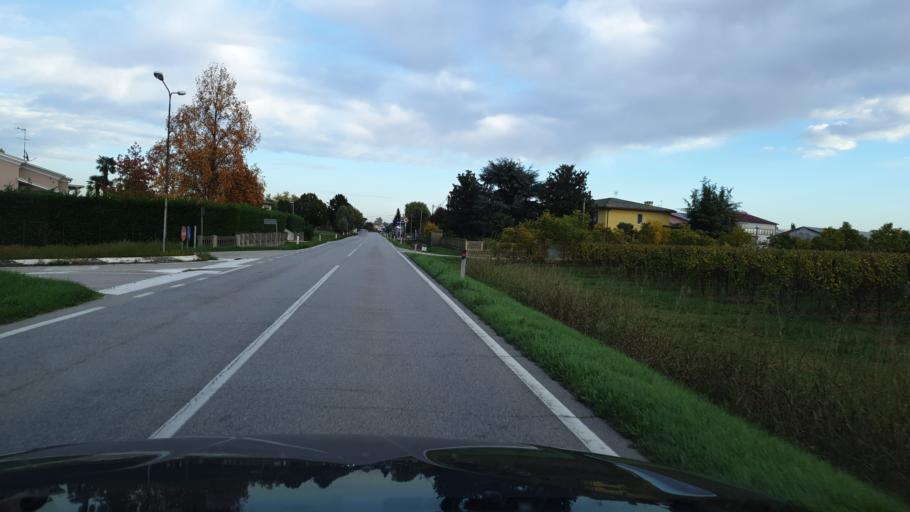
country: IT
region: Veneto
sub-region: Provincia di Padova
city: San Pietro Viminario
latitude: 45.2291
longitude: 11.8112
